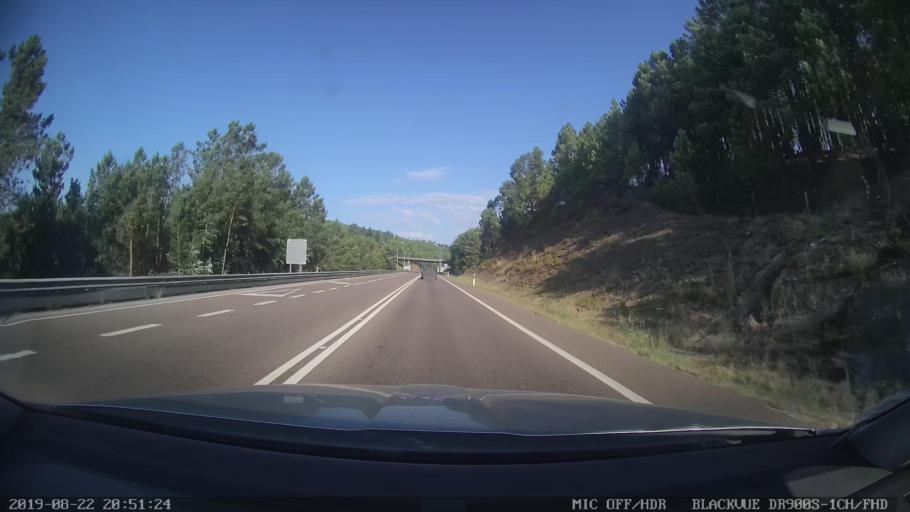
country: PT
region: Castelo Branco
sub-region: Proenca-A-Nova
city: Proenca-a-Nova
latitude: 39.7596
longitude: -7.9587
